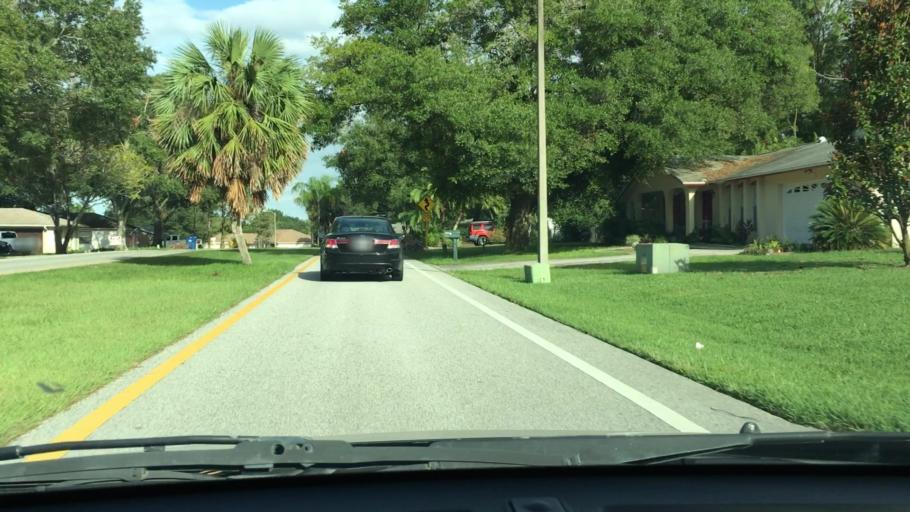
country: US
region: Florida
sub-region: Pasco County
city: Land O' Lakes
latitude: 28.2116
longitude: -82.4314
